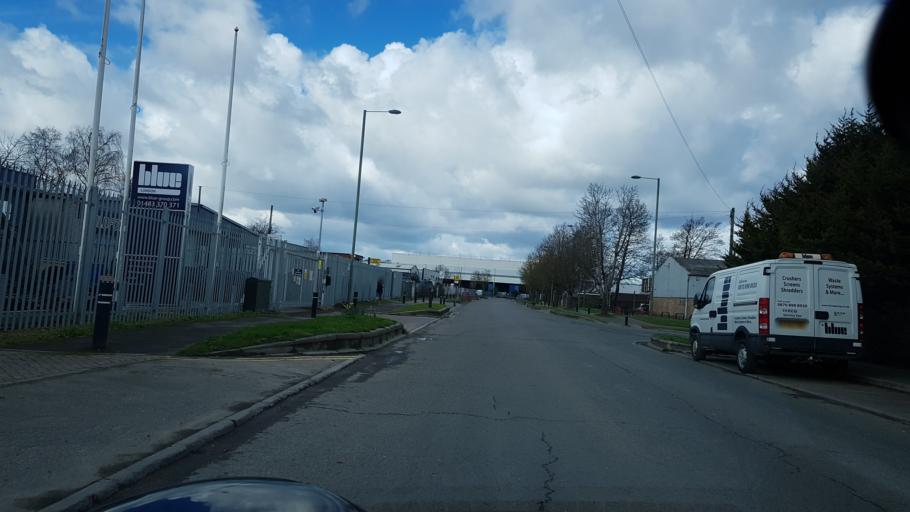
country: GB
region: England
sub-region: Surrey
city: Guildford
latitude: 51.2622
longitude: -0.5640
